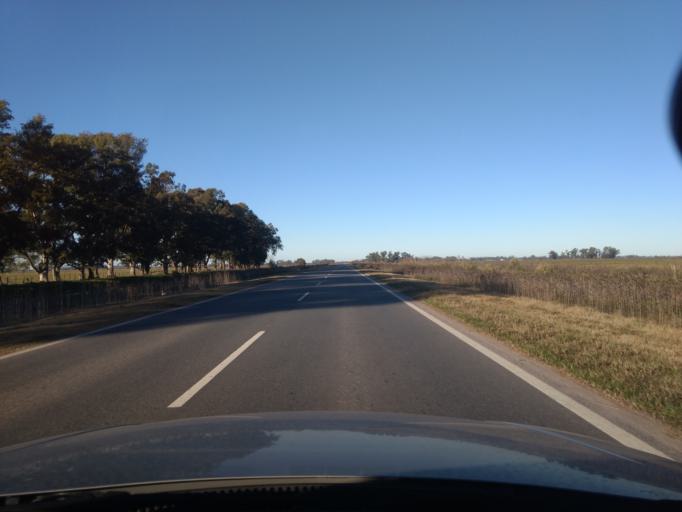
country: AR
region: Buenos Aires
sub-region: Partido de Navarro
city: Navarro
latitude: -34.8924
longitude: -59.2200
